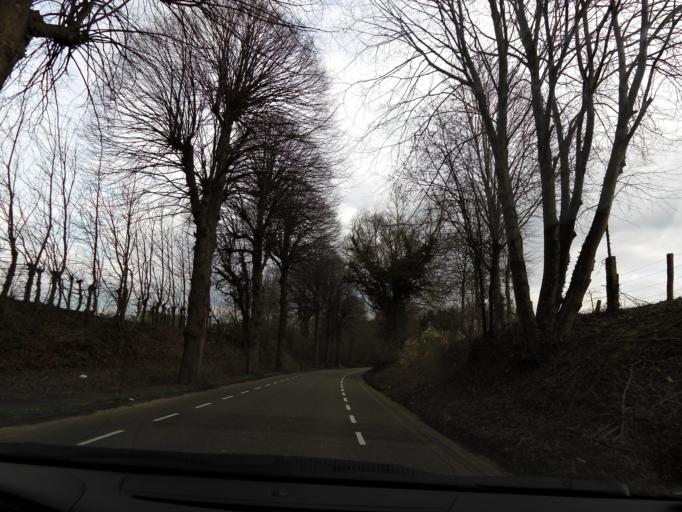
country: NL
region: Limburg
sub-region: Valkenburg aan de Geul
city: Sibbe
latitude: 50.8530
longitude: 5.8220
